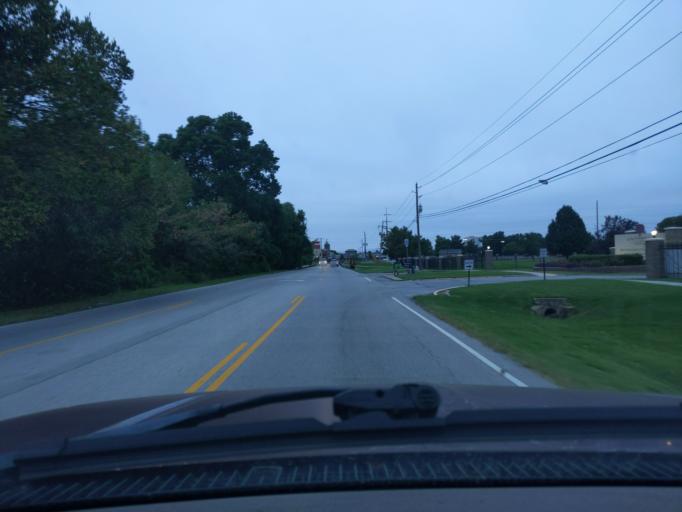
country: US
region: Oklahoma
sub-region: Tulsa County
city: Jenks
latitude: 36.0398
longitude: -95.9567
